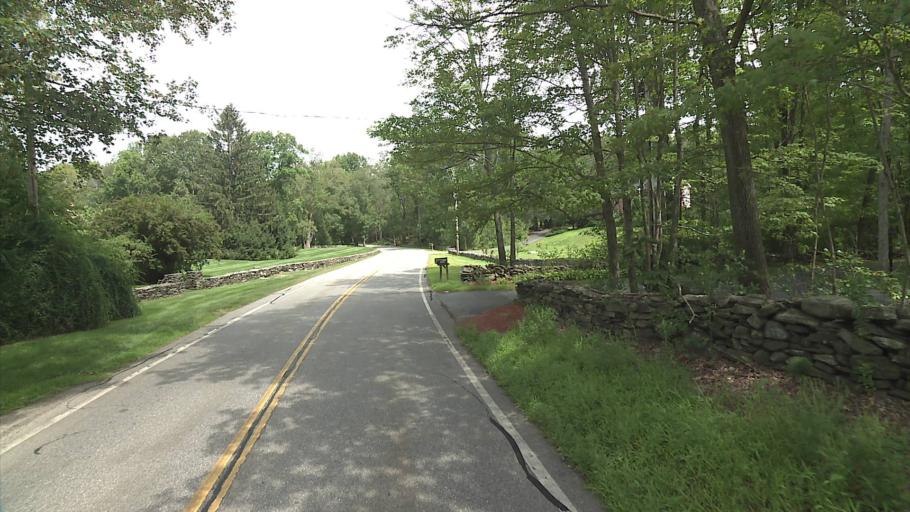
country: US
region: Connecticut
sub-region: Windham County
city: Thompson
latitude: 41.9462
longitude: -71.8647
